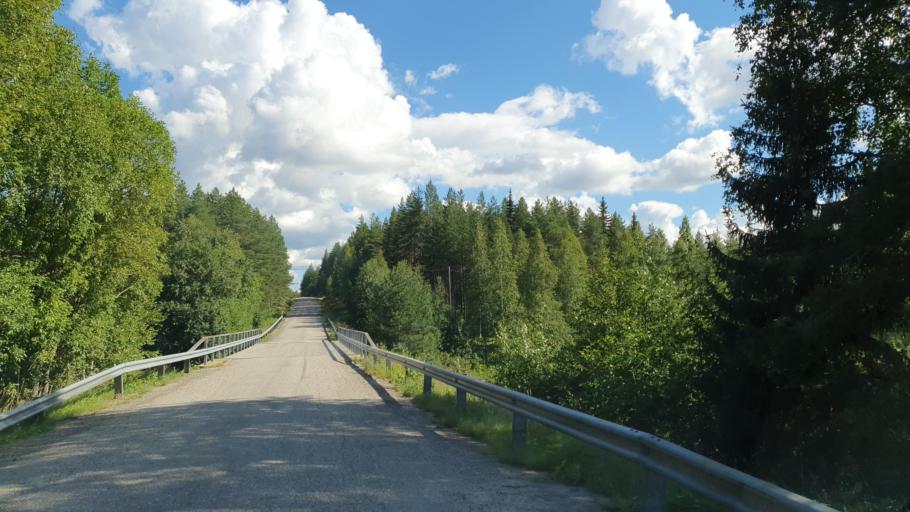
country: FI
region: Kainuu
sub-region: Kehys-Kainuu
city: Kuhmo
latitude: 64.1088
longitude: 29.3850
